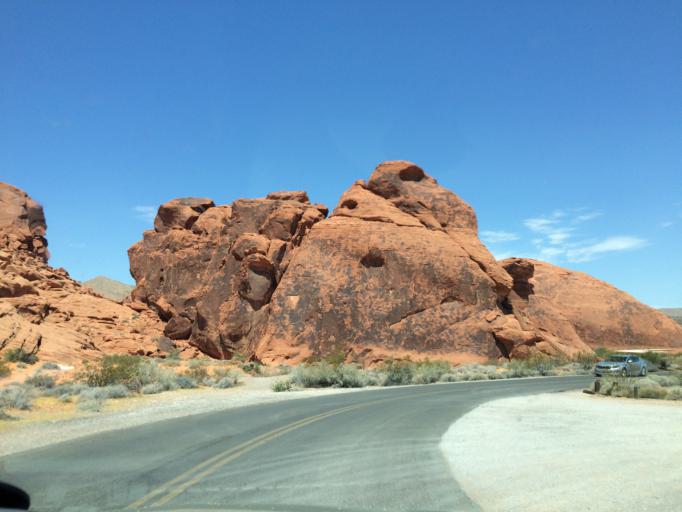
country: US
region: Nevada
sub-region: Clark County
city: Moapa Valley
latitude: 36.4223
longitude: -114.5494
